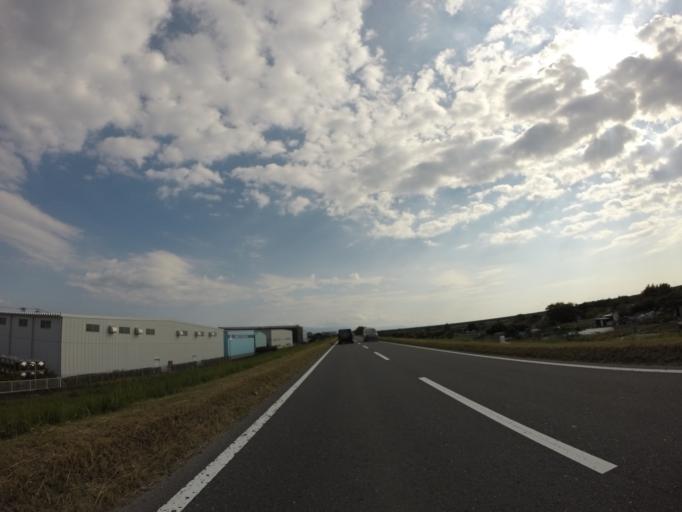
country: JP
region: Shizuoka
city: Fuji
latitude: 35.1350
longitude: 138.6398
